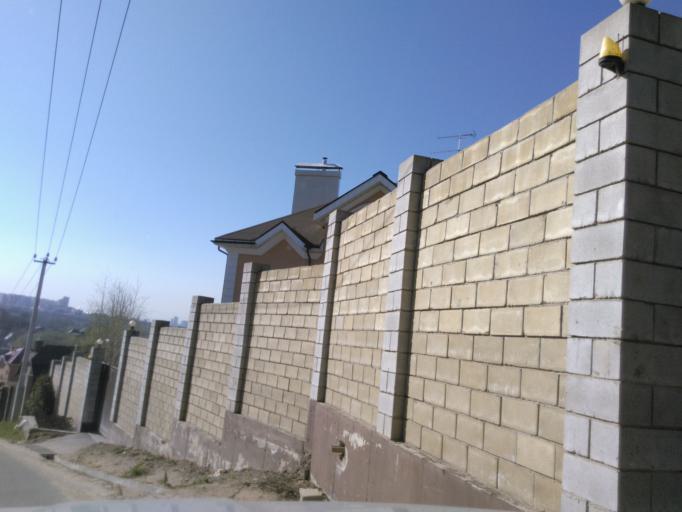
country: RU
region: Moscow
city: Khimki
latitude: 55.8794
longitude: 37.3738
